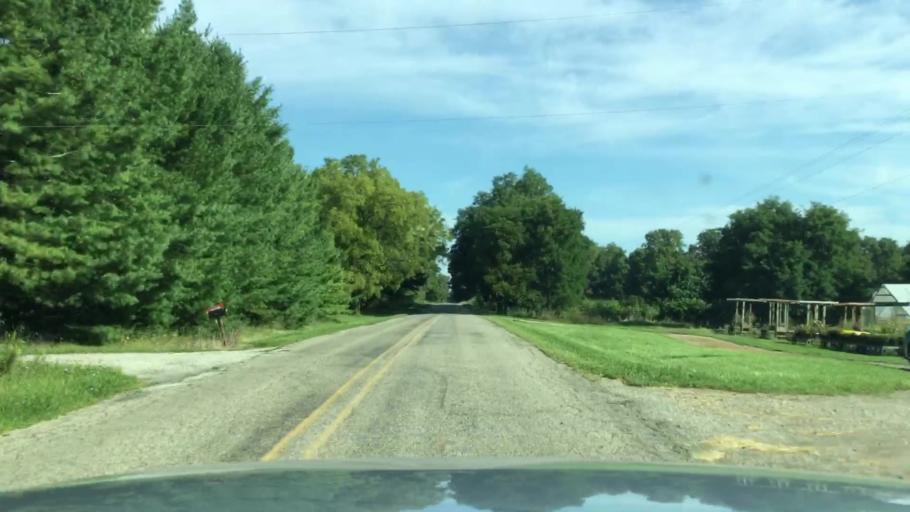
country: US
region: Michigan
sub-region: Lenawee County
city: Hudson
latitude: 41.8740
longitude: -84.4201
